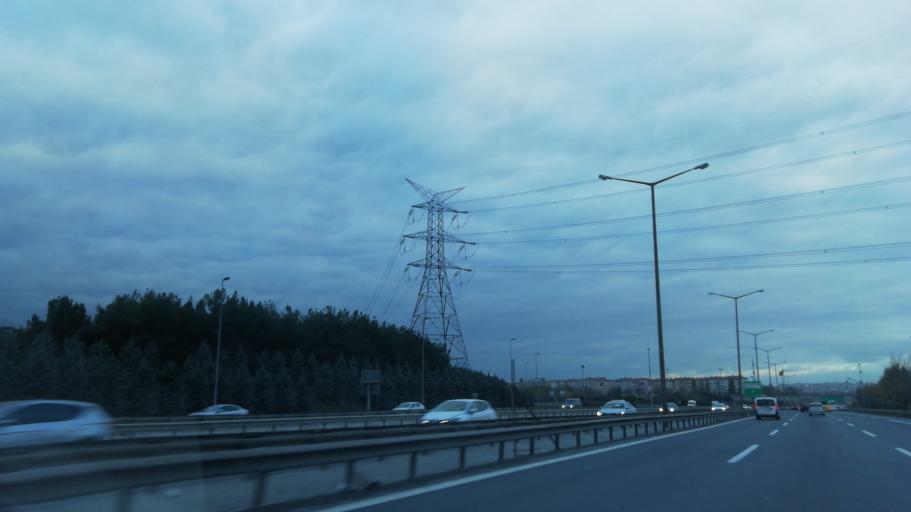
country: TR
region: Istanbul
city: Sultangazi
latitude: 41.0769
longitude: 28.8714
